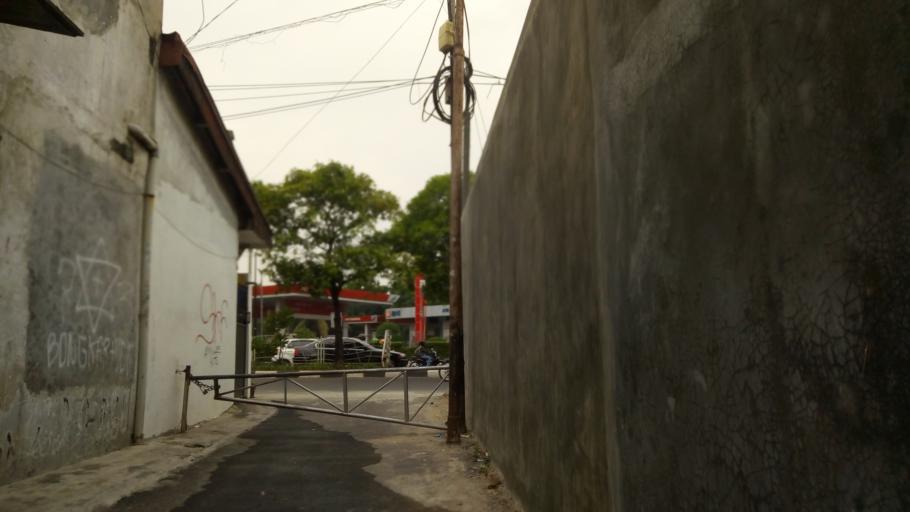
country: ID
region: Jakarta Raya
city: Jakarta
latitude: -6.1484
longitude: 106.8387
